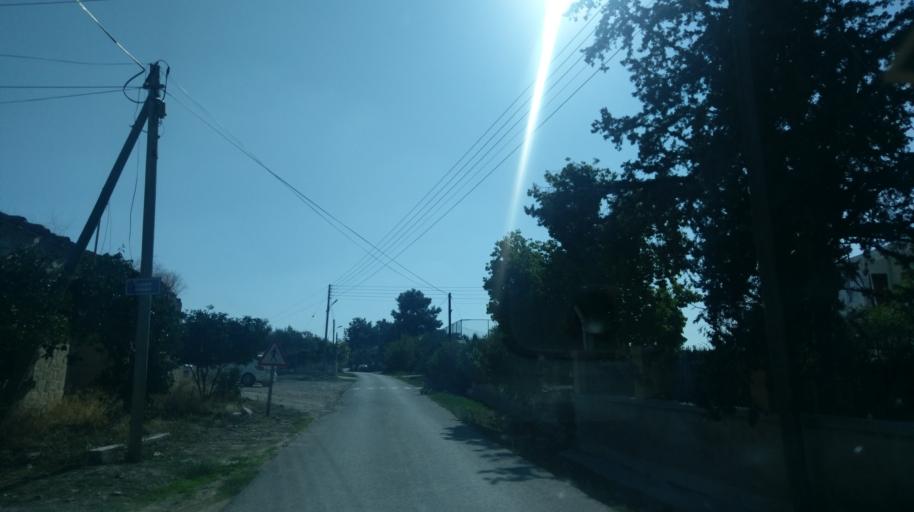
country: CY
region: Lefkosia
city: Lympia
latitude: 35.0086
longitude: 33.4642
